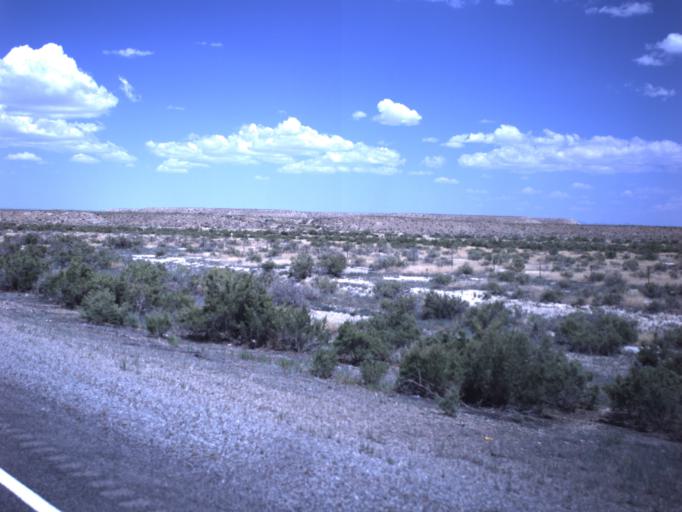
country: US
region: Utah
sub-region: Emery County
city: Huntington
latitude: 39.3820
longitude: -110.9075
